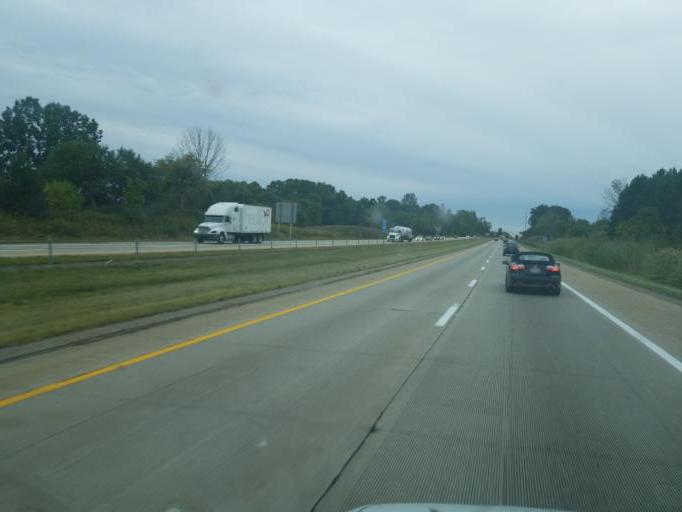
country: US
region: Ohio
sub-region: Portage County
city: Brimfield
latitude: 41.0952
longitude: -81.3823
